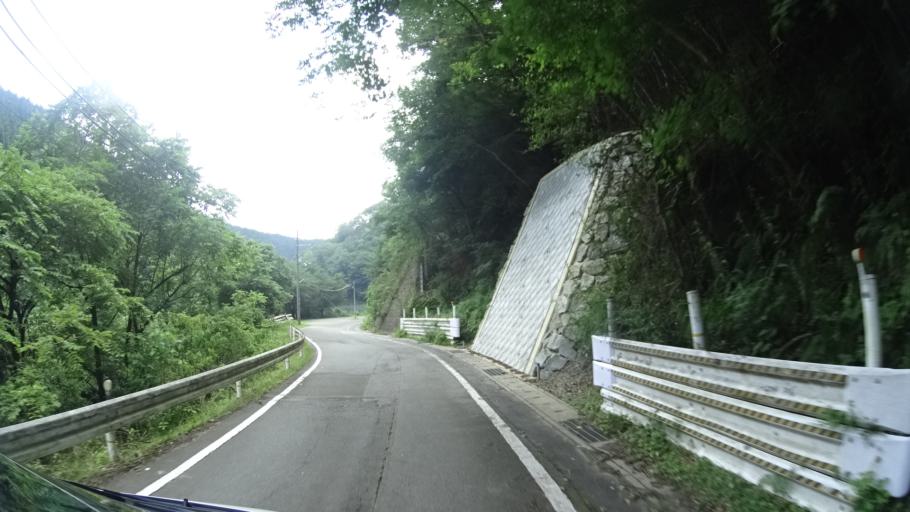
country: JP
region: Hyogo
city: Sasayama
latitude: 35.1820
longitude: 135.2171
